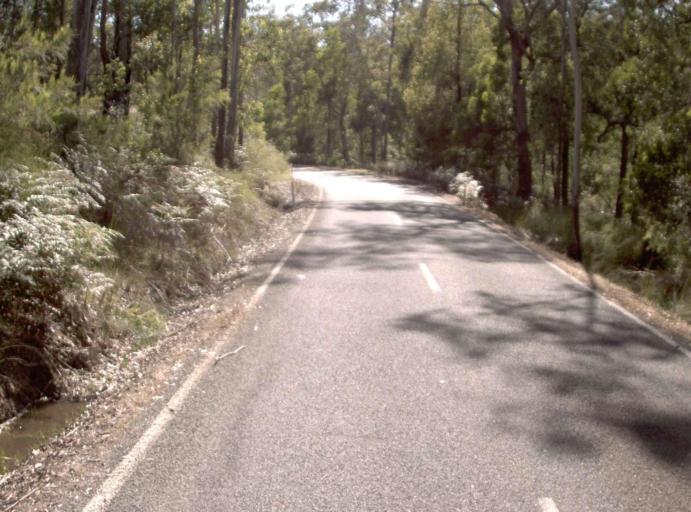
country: AU
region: New South Wales
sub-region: Bombala
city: Bombala
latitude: -37.3835
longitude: 148.6532
